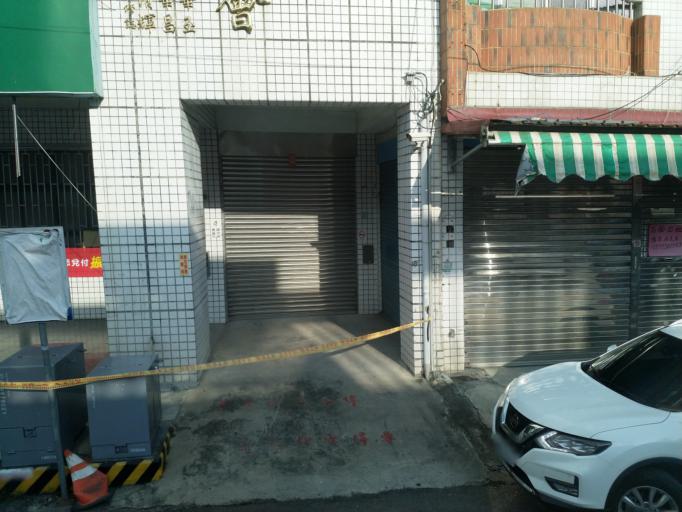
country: TW
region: Taiwan
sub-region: Pingtung
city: Pingtung
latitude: 22.9020
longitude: 120.5413
